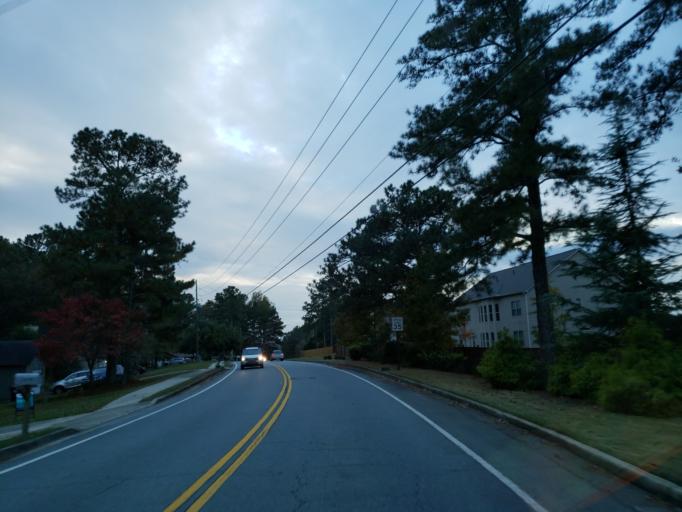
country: US
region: Georgia
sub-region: Cobb County
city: Kennesaw
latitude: 34.0230
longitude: -84.6544
